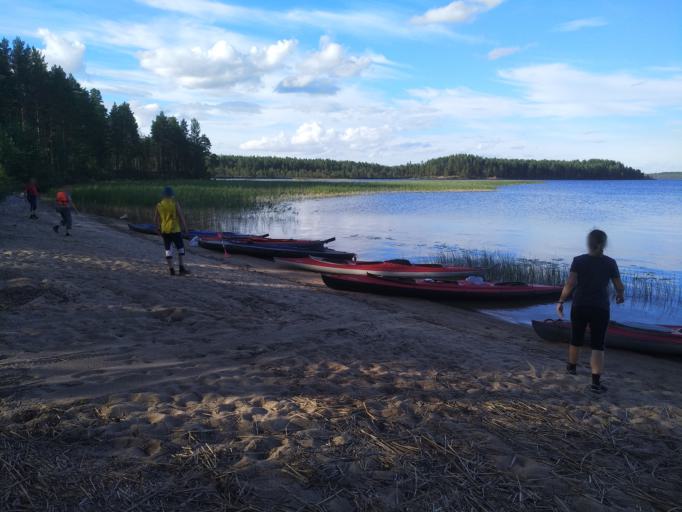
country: RU
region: Republic of Karelia
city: Kalevala
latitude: 64.8781
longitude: 31.1099
